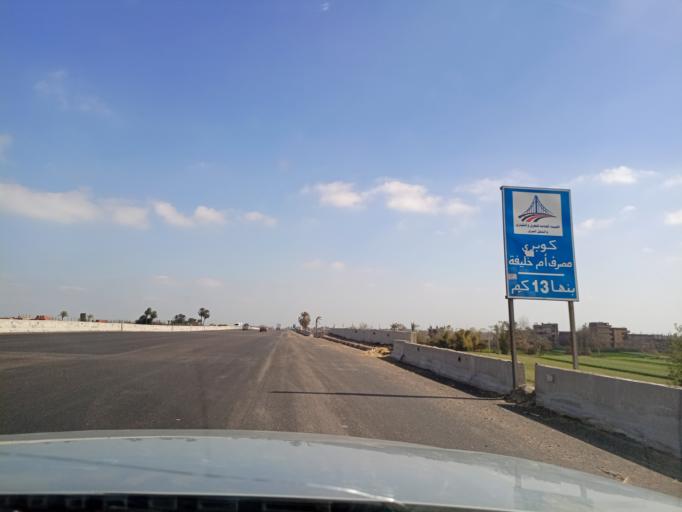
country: EG
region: Muhafazat al Minufiyah
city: Al Bajur
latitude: 30.4111
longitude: 31.0574
